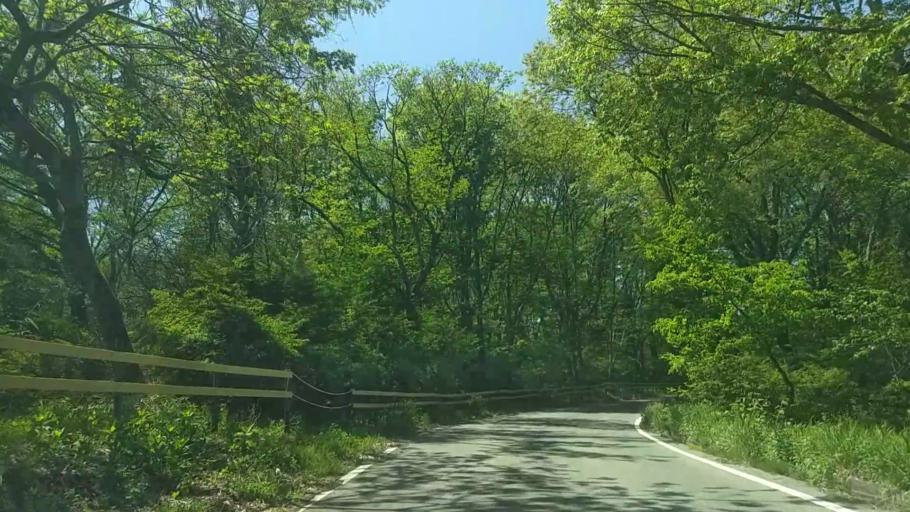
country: JP
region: Yamanashi
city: Nirasaki
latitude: 35.9010
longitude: 138.4486
